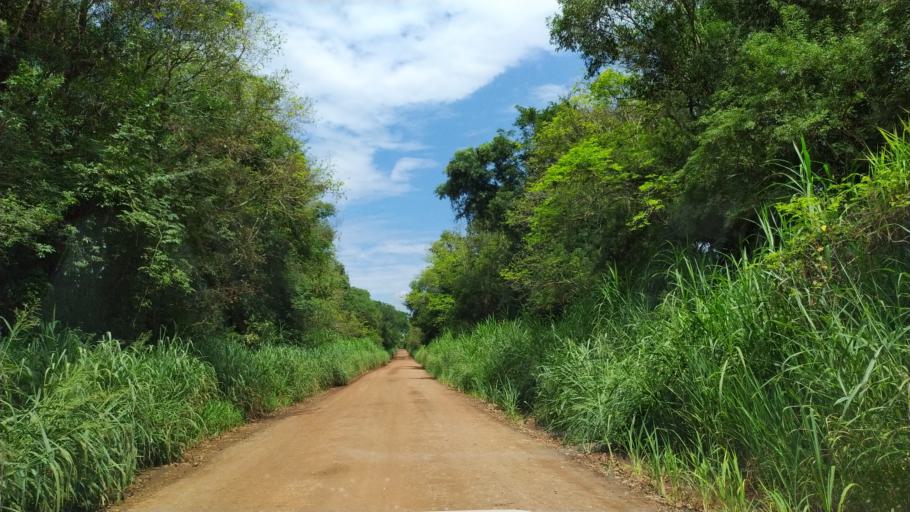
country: AR
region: Misiones
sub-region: Departamento de Eldorado
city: Eldorado
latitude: -26.4651
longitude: -54.5934
